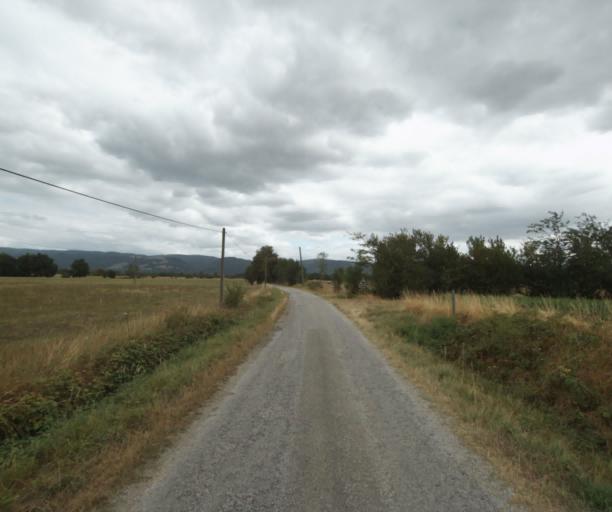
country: FR
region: Midi-Pyrenees
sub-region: Departement de la Haute-Garonne
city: Revel
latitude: 43.4801
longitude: 2.0308
